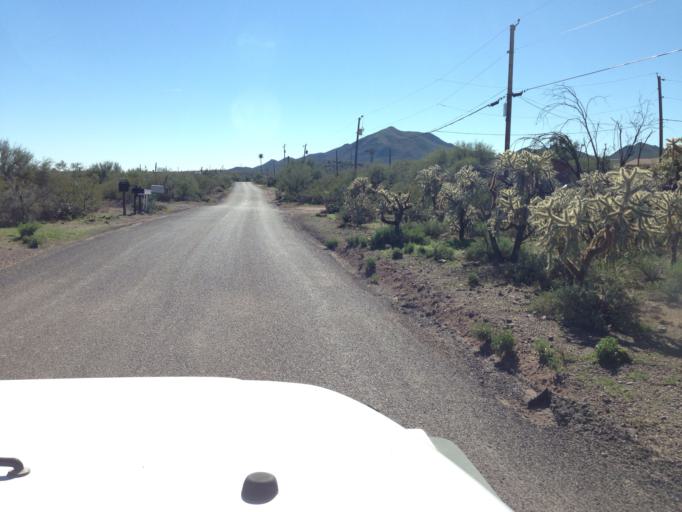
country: US
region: Arizona
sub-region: Maricopa County
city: New River
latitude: 33.9227
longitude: -112.0913
